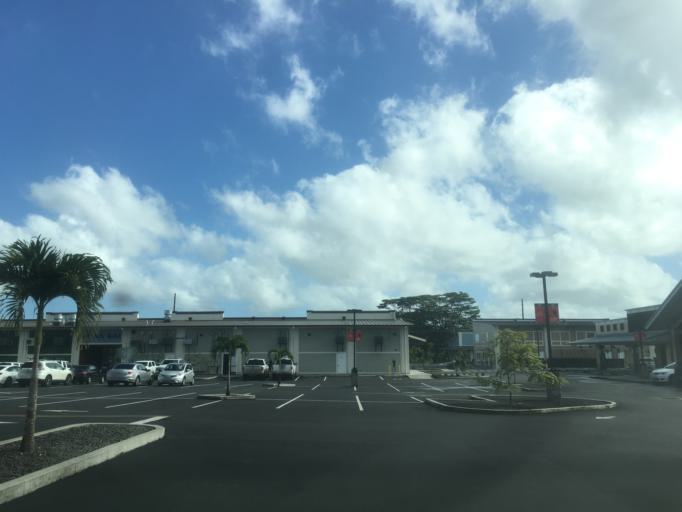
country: US
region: Hawaii
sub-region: Hawaii County
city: Hawaiian Paradise Park
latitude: 19.5024
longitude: -154.9572
